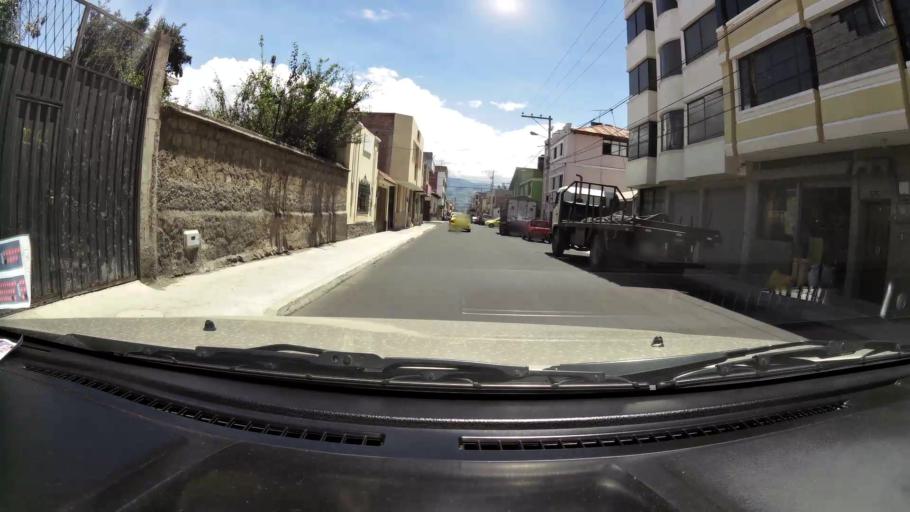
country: EC
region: Chimborazo
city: Riobamba
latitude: -1.6696
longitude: -78.6469
